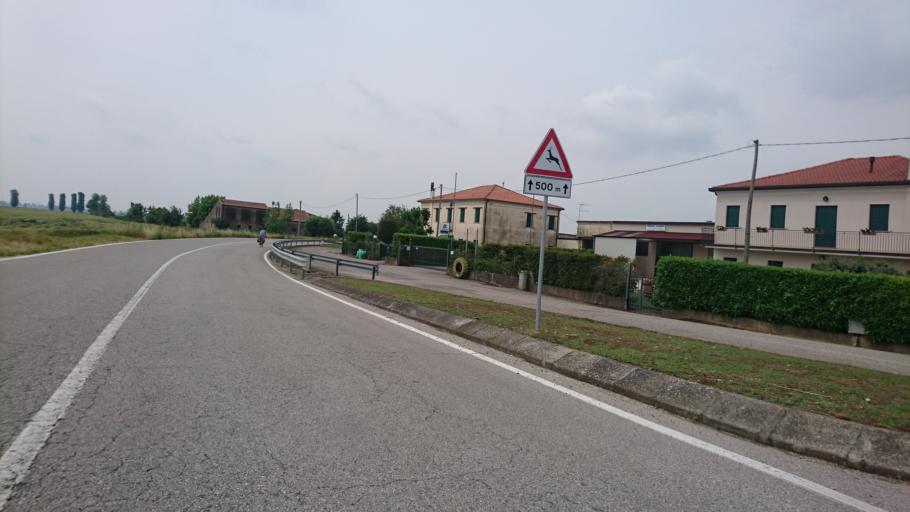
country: IT
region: Veneto
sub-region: Provincia di Padova
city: Vighizzolo d'Este
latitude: 45.1406
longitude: 11.6327
